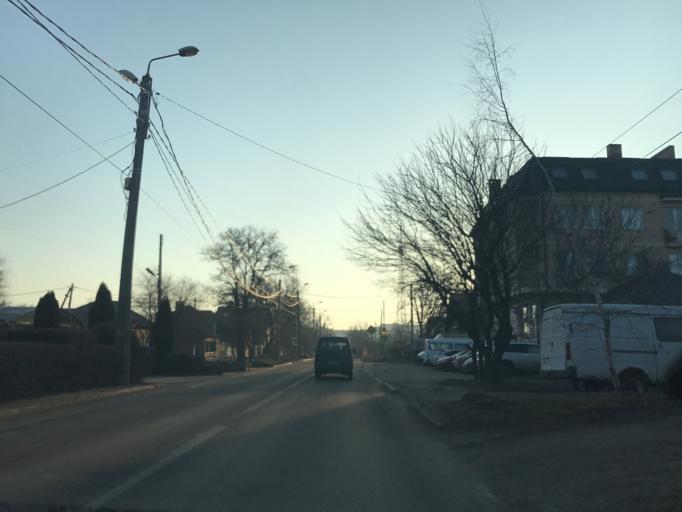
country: RU
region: Rostov
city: Rostov-na-Donu
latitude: 47.2147
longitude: 39.6682
